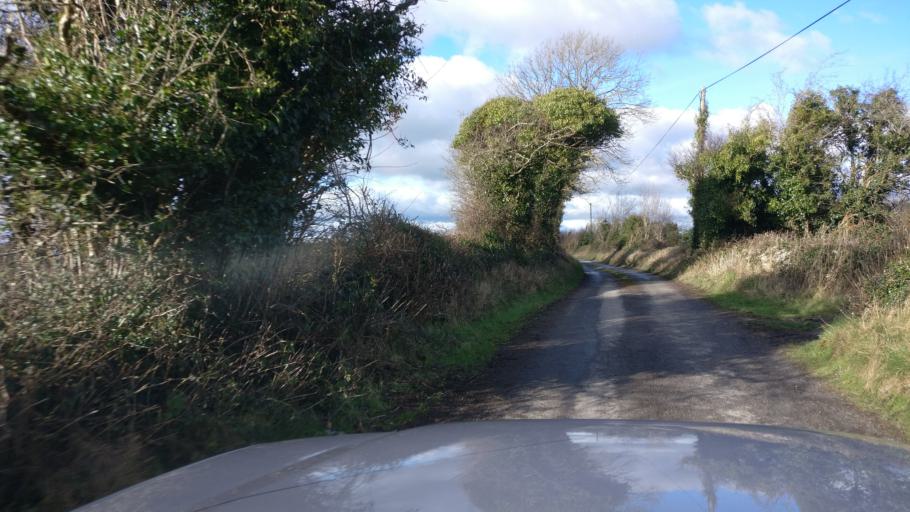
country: IE
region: Connaught
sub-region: County Galway
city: Athenry
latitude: 53.2299
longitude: -8.7998
